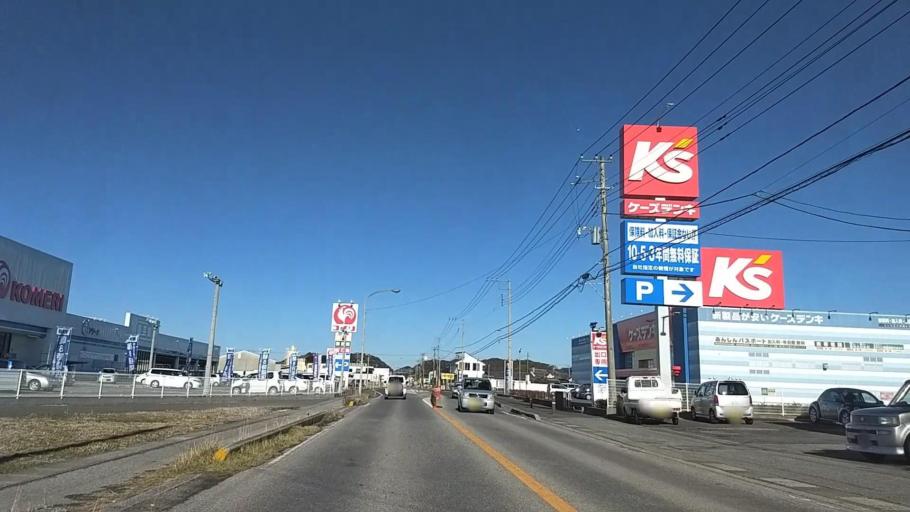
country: JP
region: Chiba
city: Ohara
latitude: 35.3011
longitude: 140.3984
